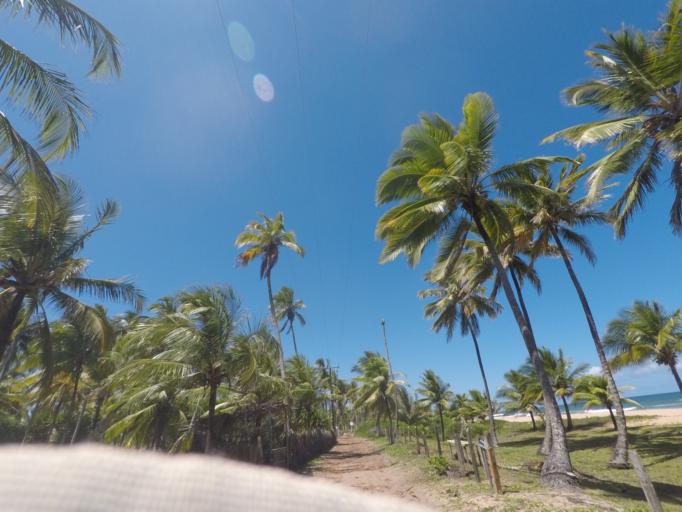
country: BR
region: Bahia
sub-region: Marau
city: Marau
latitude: -14.0044
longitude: -38.9446
